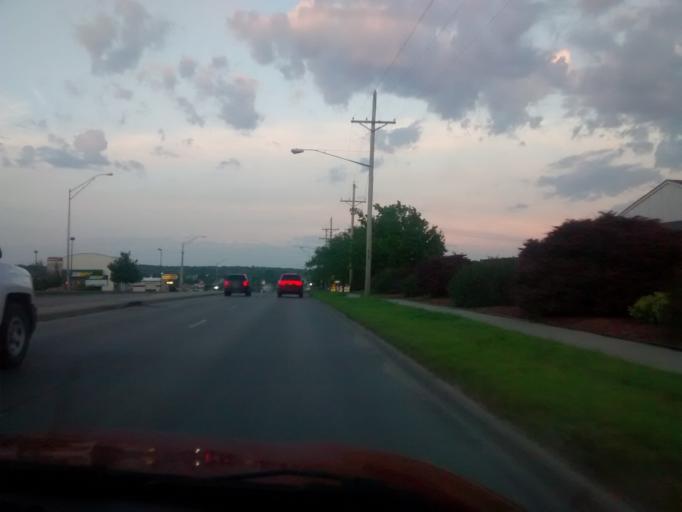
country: US
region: Nebraska
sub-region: Sarpy County
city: Offutt Air Force Base
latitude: 41.1593
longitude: -95.9472
